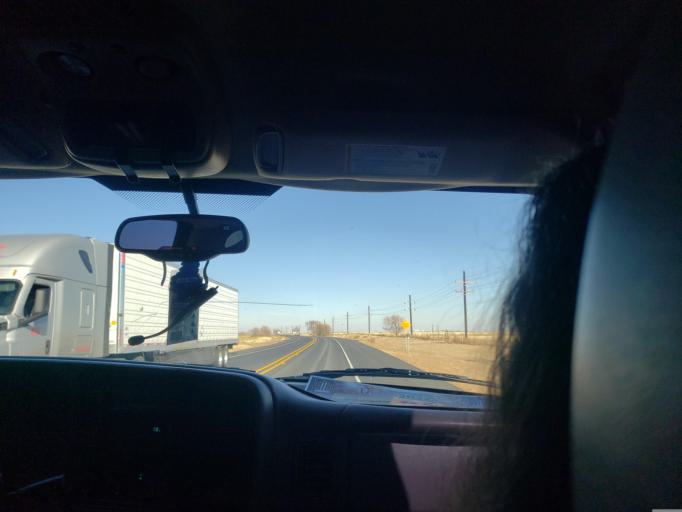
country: US
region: Texas
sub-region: Dallam County
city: Dalhart
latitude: 35.9655
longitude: -102.6464
